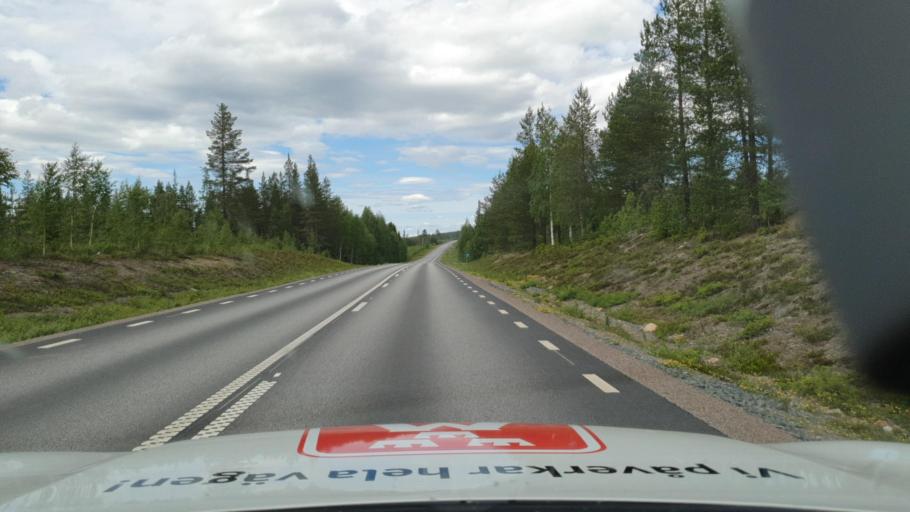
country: SE
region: Vaesterbotten
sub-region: Norsjo Kommun
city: Norsjoe
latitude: 65.1661
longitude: 19.8777
